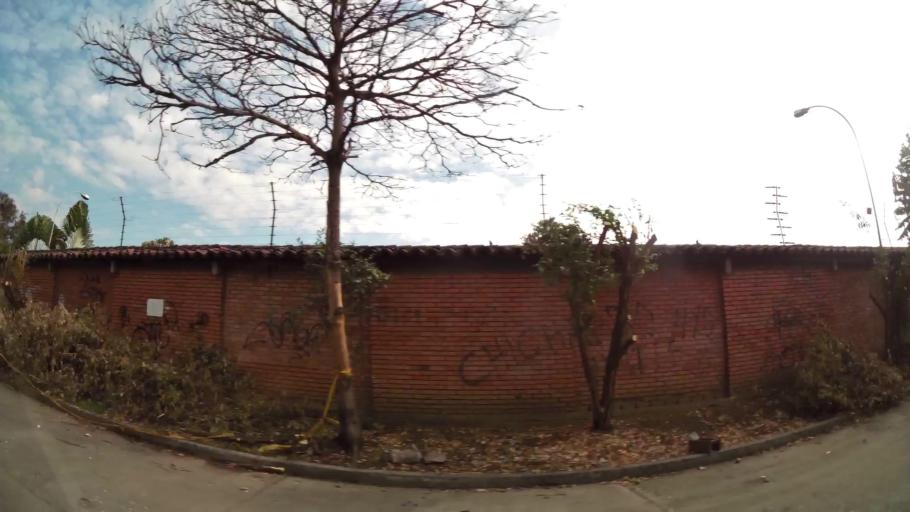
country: CO
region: Valle del Cauca
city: Cali
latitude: 3.4835
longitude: -76.4928
